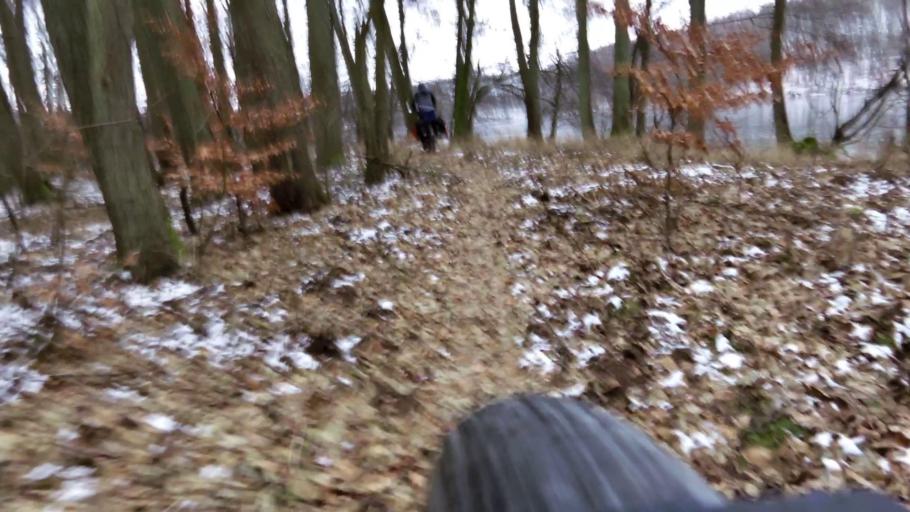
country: PL
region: West Pomeranian Voivodeship
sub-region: Powiat walecki
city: Miroslawiec
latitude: 53.3511
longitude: 16.2603
